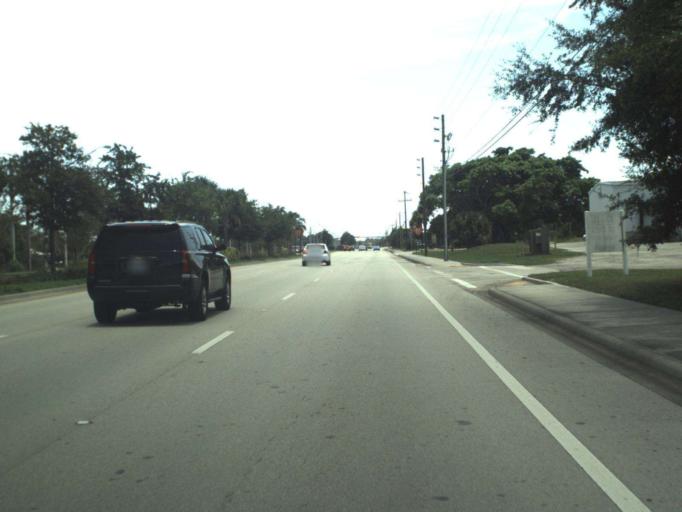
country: US
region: Florida
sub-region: Indian River County
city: Florida Ridge
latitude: 27.5922
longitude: -80.3794
